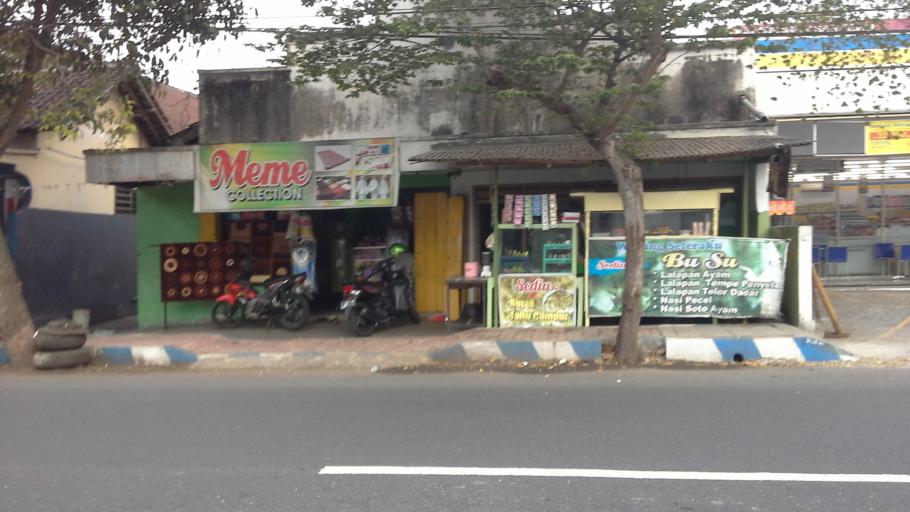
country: ID
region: East Java
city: Bondowoso
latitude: -7.9219
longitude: 113.8272
